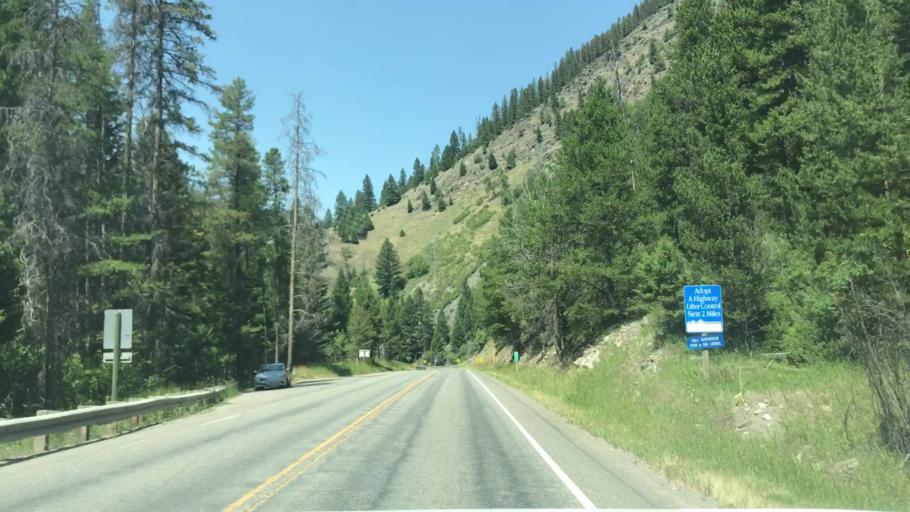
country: US
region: Montana
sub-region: Gallatin County
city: Big Sky
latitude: 45.4052
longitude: -111.2198
